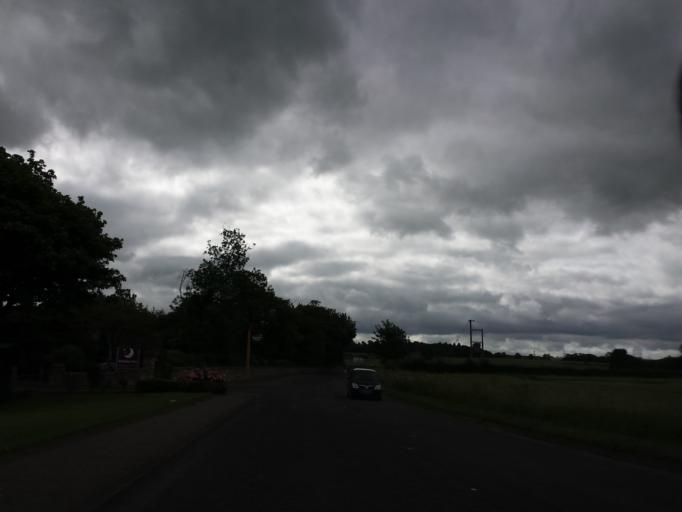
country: GB
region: Scotland
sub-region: East Lothian
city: Musselburgh
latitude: 55.9257
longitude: -3.0361
